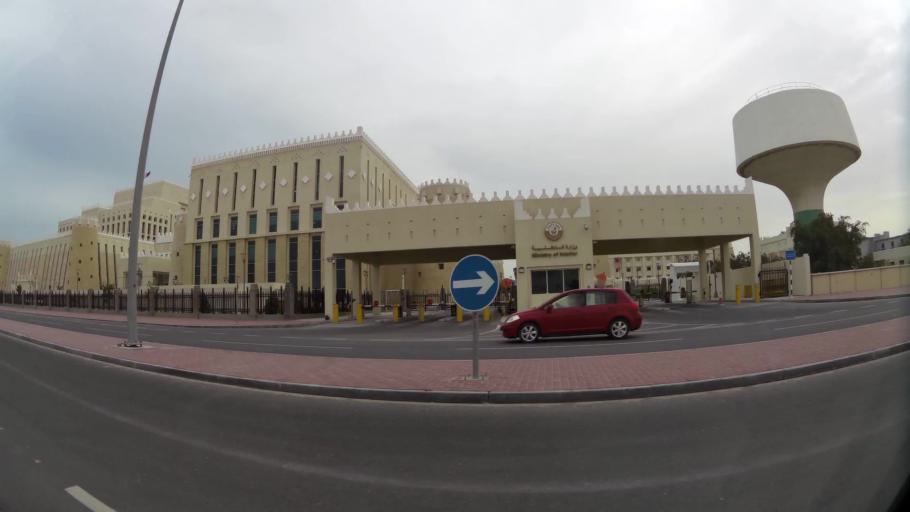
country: QA
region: Baladiyat ad Dawhah
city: Doha
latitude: 25.3059
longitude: 51.5011
